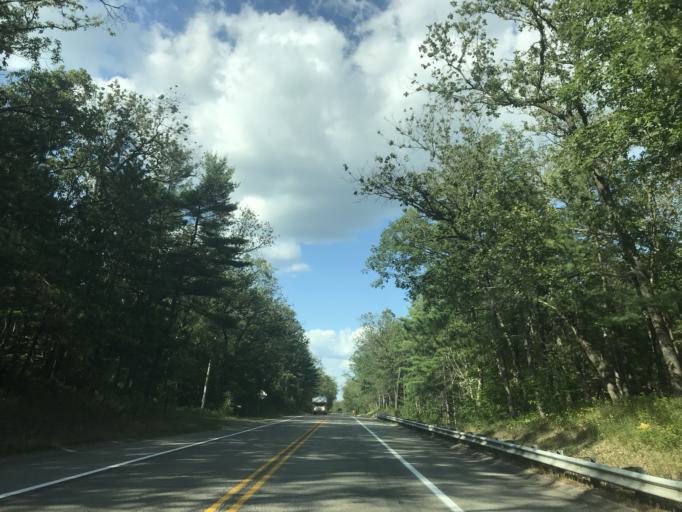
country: US
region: Michigan
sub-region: Newaygo County
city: Newaygo
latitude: 43.4603
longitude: -85.7778
